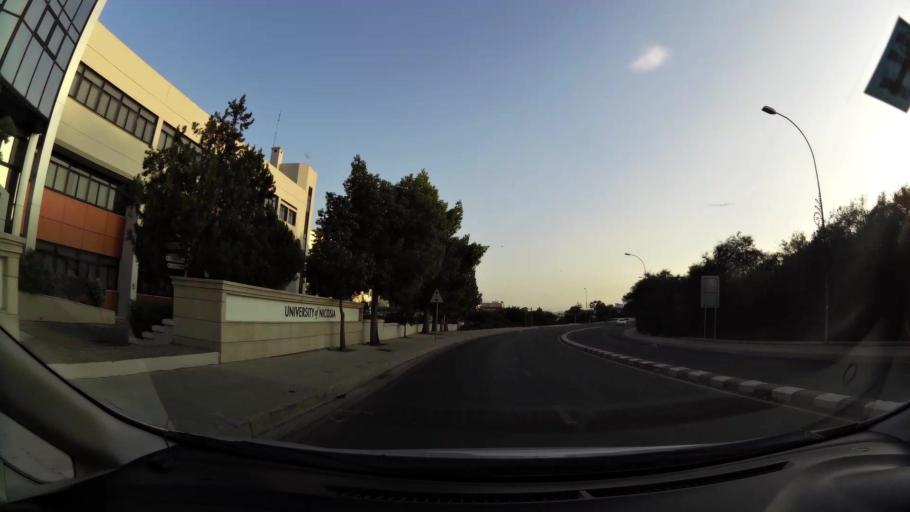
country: CY
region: Lefkosia
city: Nicosia
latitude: 35.1658
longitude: 33.3141
